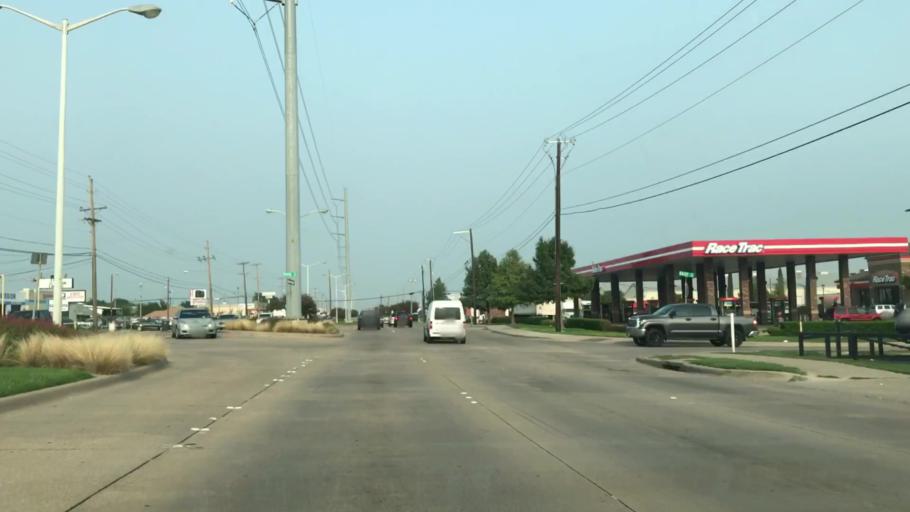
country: US
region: Texas
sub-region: Dallas County
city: Richardson
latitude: 32.9090
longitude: -96.6936
